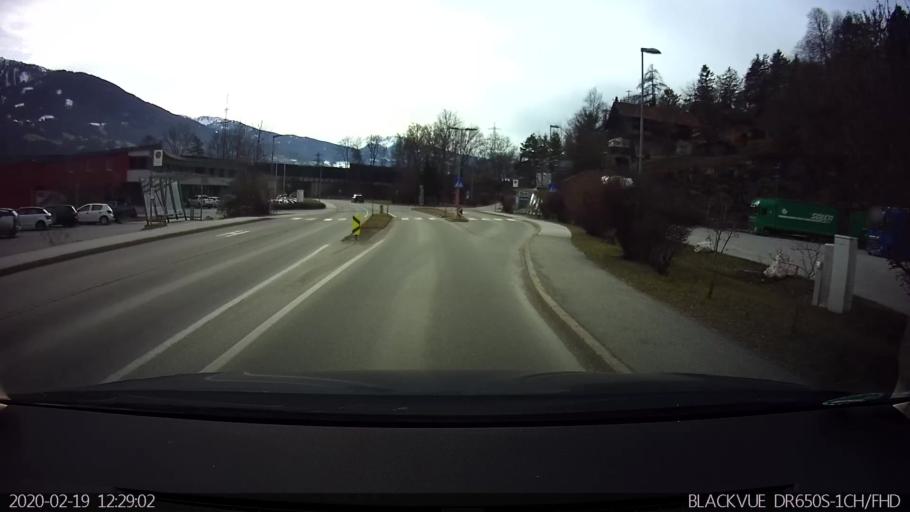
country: AT
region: Tyrol
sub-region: Politischer Bezirk Schwaz
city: Stans
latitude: 47.3634
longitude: 11.7107
